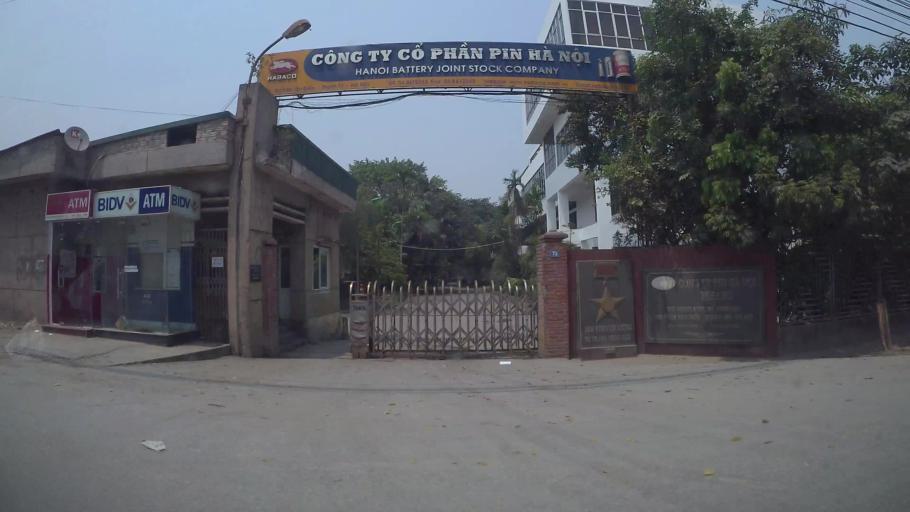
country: VN
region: Ha Noi
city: Van Dien
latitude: 20.9435
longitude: 105.8415
